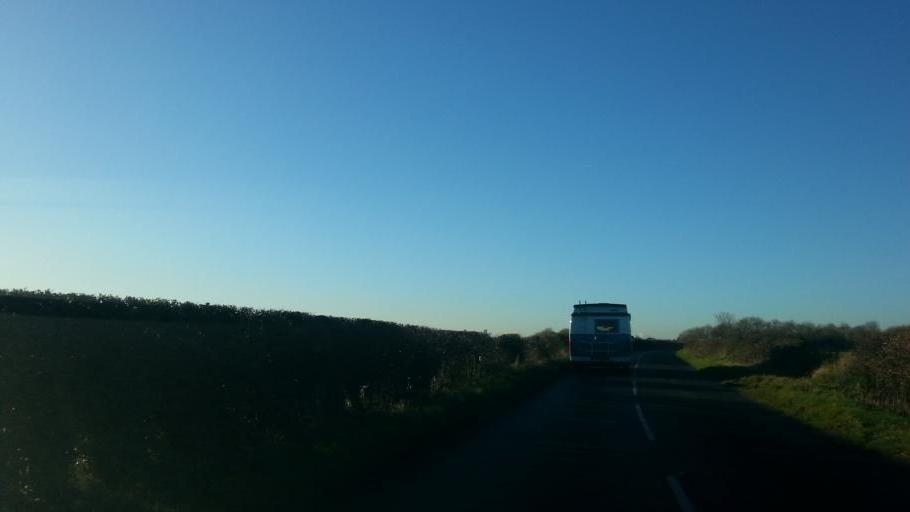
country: GB
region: England
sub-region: Nottinghamshire
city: Newark on Trent
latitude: 53.1026
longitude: -0.8274
